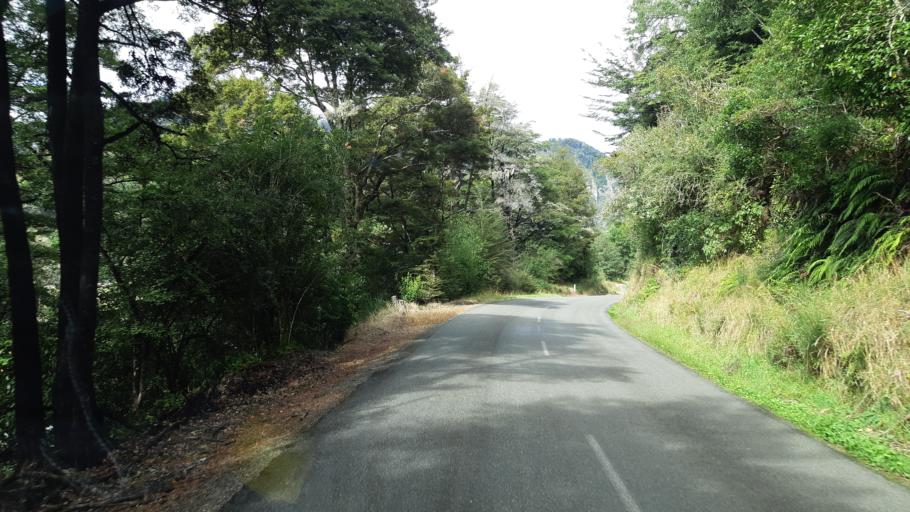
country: NZ
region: West Coast
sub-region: Buller District
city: Westport
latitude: -41.7856
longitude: 172.3677
